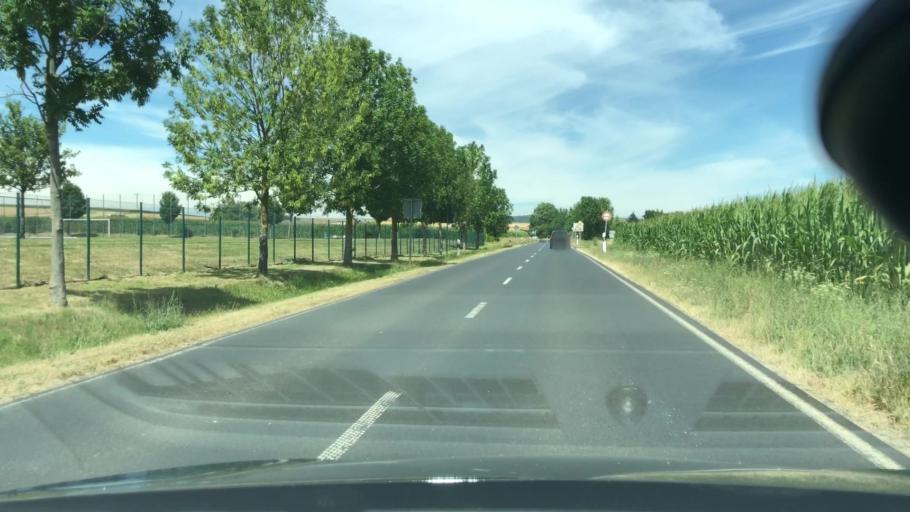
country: DE
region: Hesse
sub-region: Regierungsbezirk Darmstadt
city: Langenselbold
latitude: 50.1894
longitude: 9.0440
